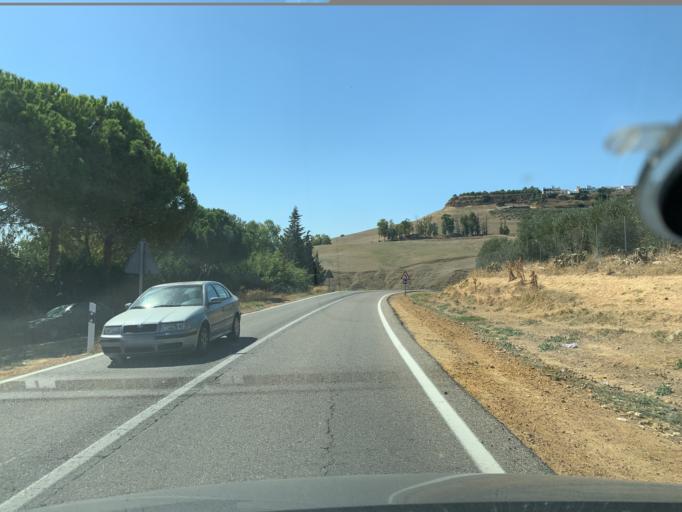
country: ES
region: Andalusia
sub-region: Provincia de Sevilla
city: Carmona
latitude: 37.4658
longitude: -5.6340
